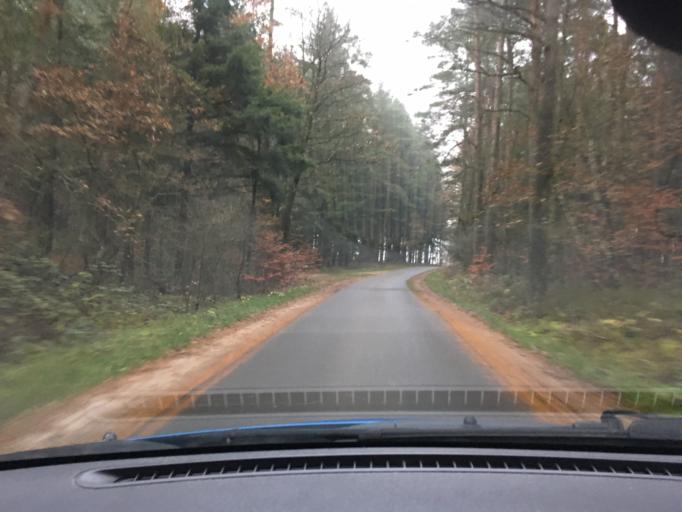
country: DE
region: Lower Saxony
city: Amelinghausen
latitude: 53.1035
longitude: 10.1873
